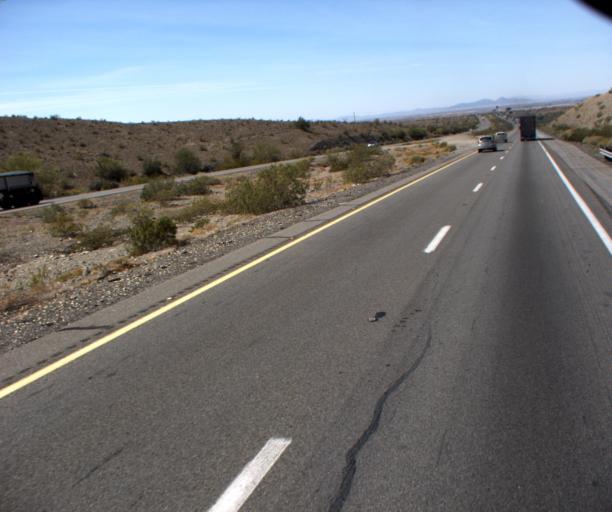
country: US
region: Arizona
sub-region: La Paz County
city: Ehrenberg
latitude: 33.6308
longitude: -114.4103
